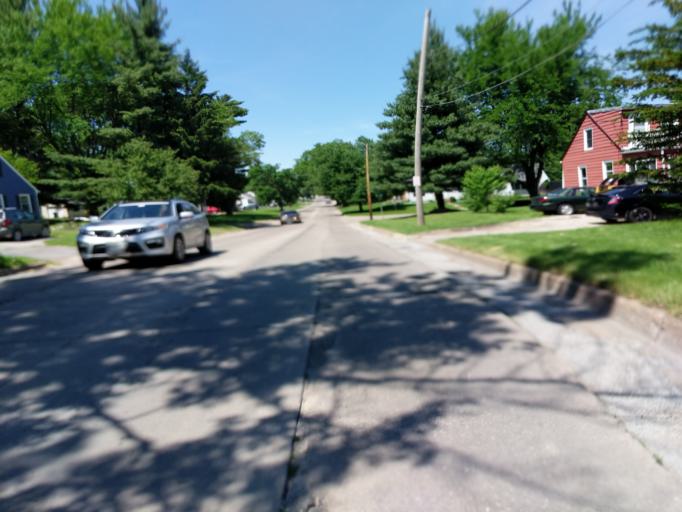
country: US
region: Iowa
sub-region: Linn County
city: Cedar Rapids
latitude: 42.0155
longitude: -91.6384
